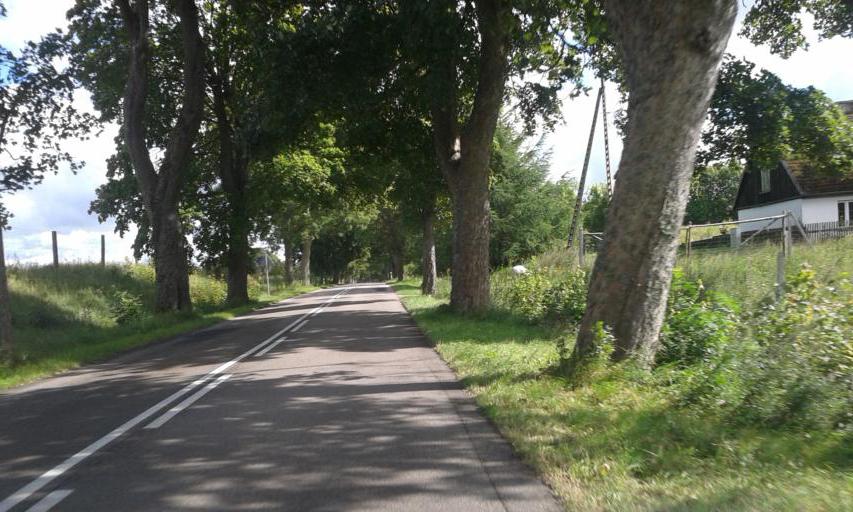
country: PL
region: West Pomeranian Voivodeship
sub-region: Powiat koszalinski
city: Bobolice
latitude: 53.9748
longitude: 16.6639
